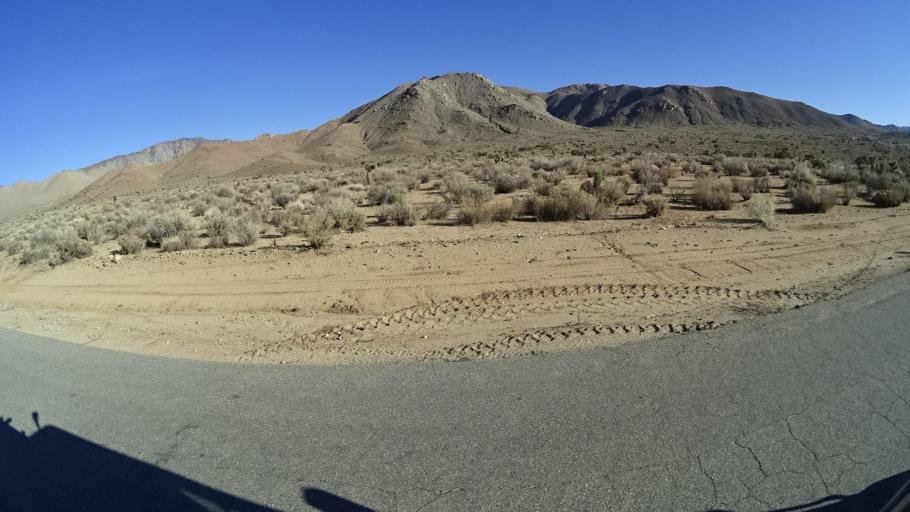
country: US
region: California
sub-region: Kern County
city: Weldon
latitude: 35.5474
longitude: -118.2061
